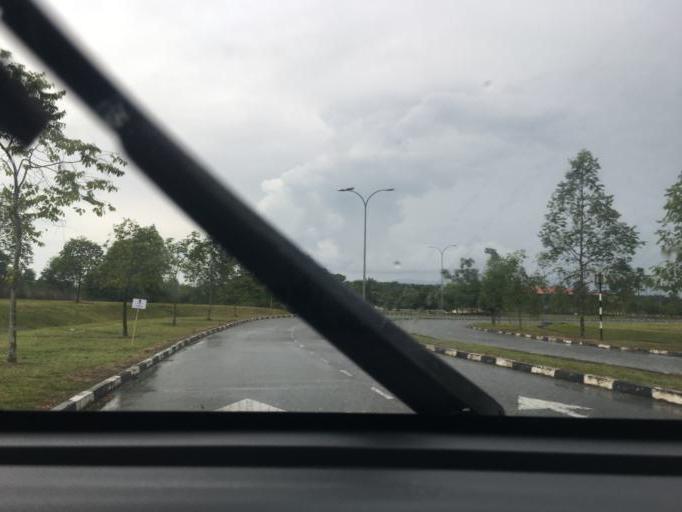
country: MY
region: Kedah
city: Sungai Petani
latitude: 5.5899
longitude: 100.6399
